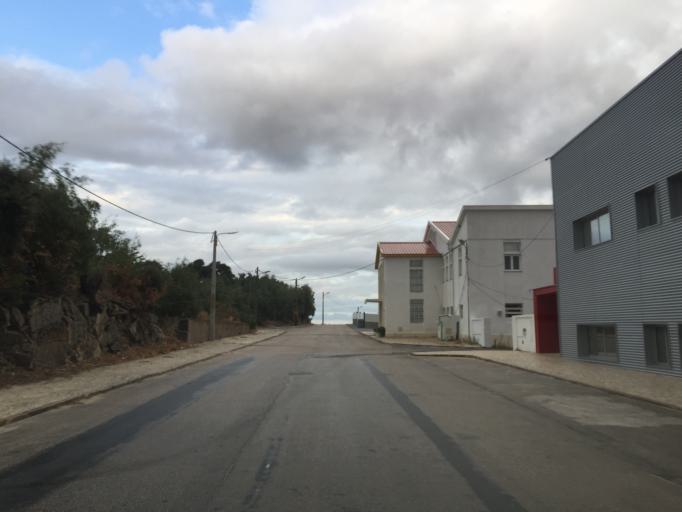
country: PT
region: Portalegre
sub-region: Marvao
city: Marvao
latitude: 39.4134
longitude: -7.3465
